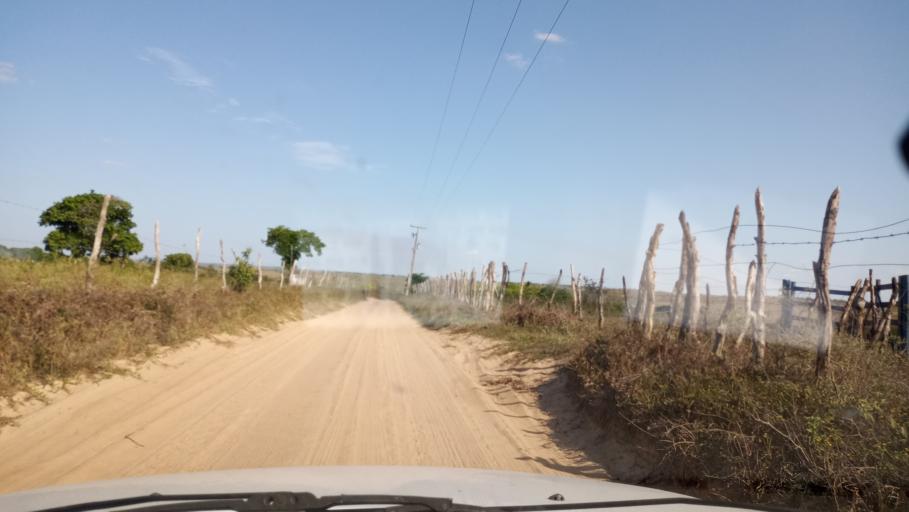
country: BR
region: Rio Grande do Norte
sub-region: Brejinho
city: Brejinho
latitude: -6.1781
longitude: -35.4549
